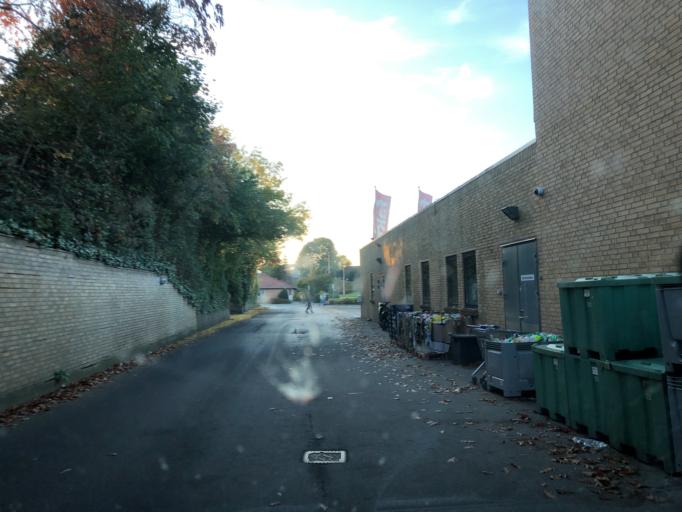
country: DK
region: South Denmark
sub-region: Vejle Kommune
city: Borkop
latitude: 55.6410
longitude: 9.6497
